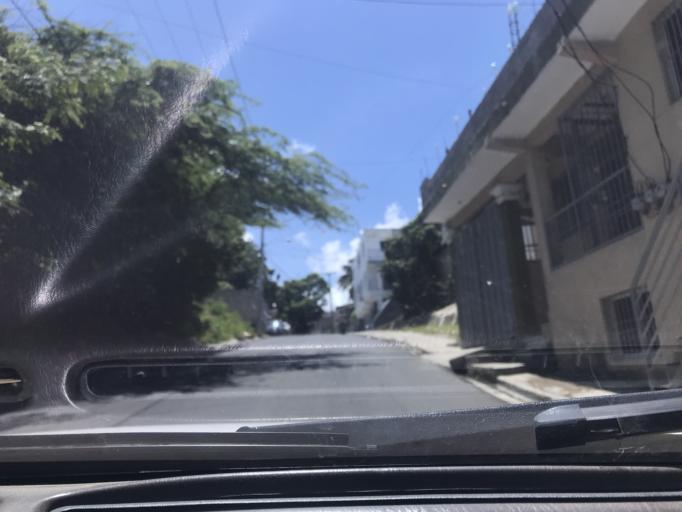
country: DO
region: Santiago
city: Santiago de los Caballeros
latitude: 19.4296
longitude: -70.6971
